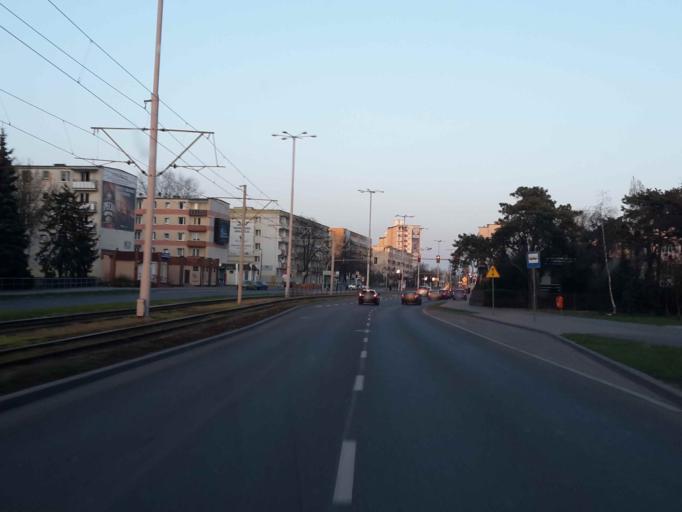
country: PL
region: Kujawsko-Pomorskie
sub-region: Torun
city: Torun
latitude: 53.0142
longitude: 18.5889
